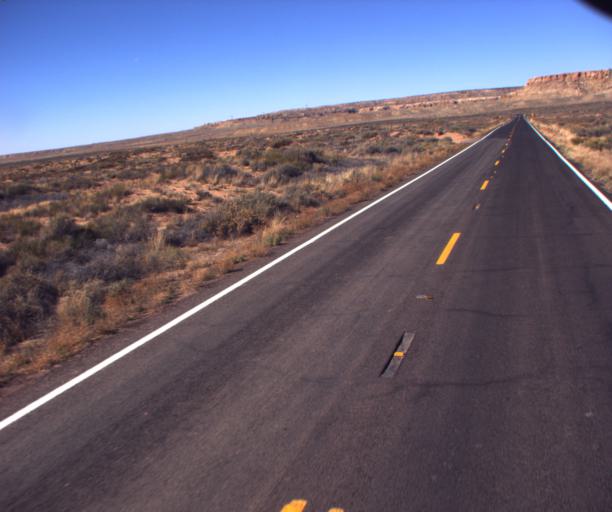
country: US
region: Arizona
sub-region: Navajo County
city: First Mesa
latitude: 35.9792
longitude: -110.7031
